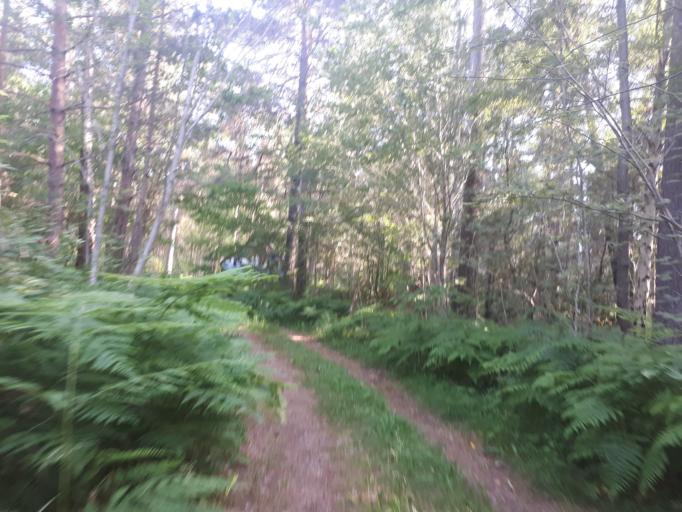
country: SE
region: Gotland
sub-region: Gotland
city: Visby
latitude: 57.6089
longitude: 18.2889
